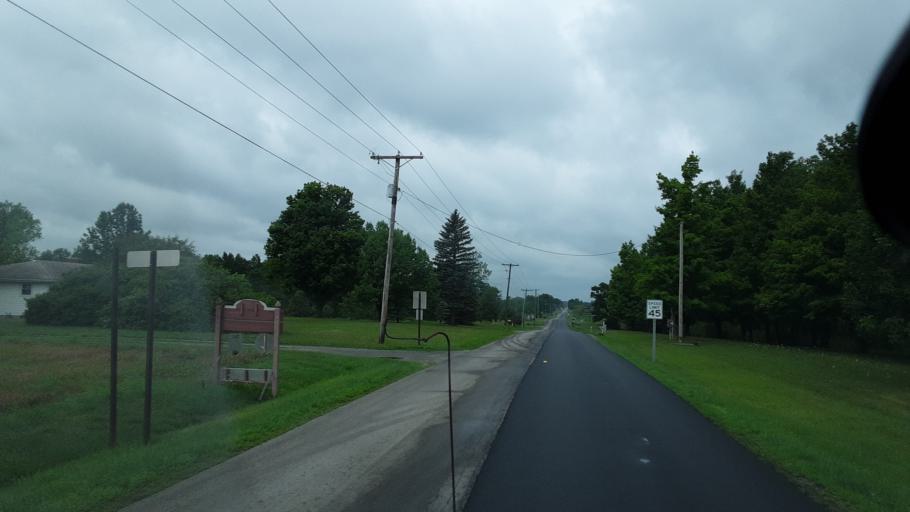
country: US
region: Indiana
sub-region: Allen County
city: New Haven
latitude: 40.9478
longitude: -85.0041
